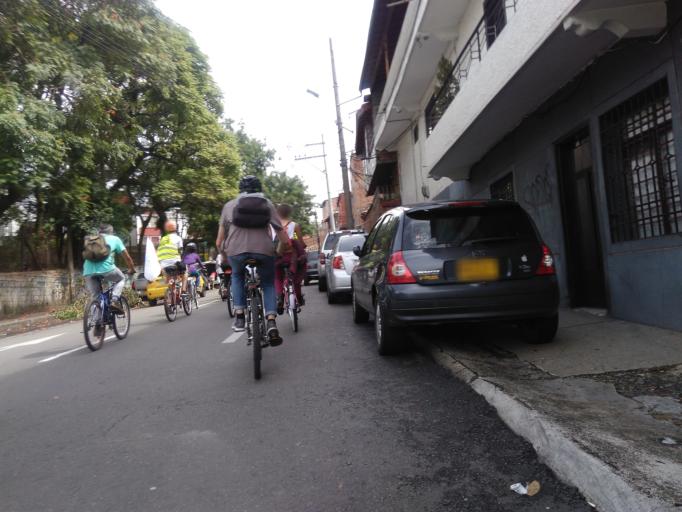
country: CO
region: Antioquia
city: Medellin
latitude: 6.2804
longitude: -75.5629
